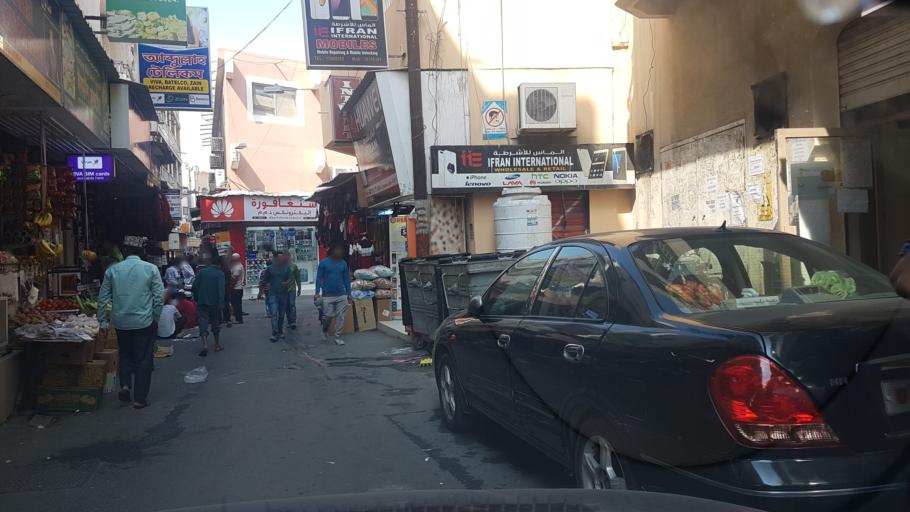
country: BH
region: Manama
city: Manama
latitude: 26.2298
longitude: 50.5745
